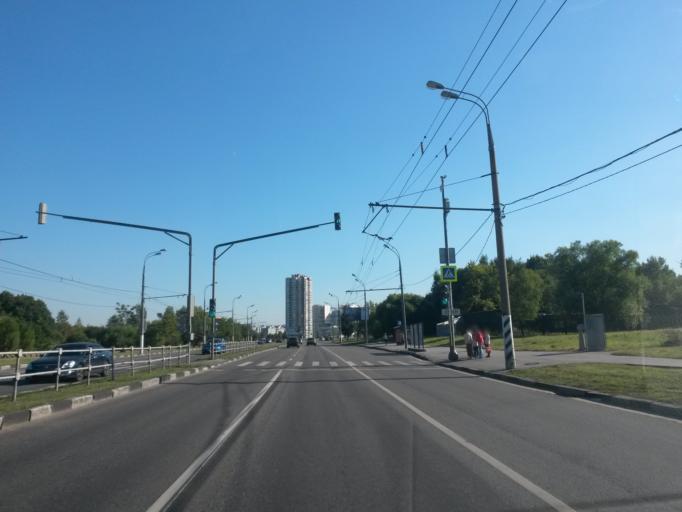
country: RU
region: Moscow
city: Yasenevo
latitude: 55.6251
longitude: 37.5418
